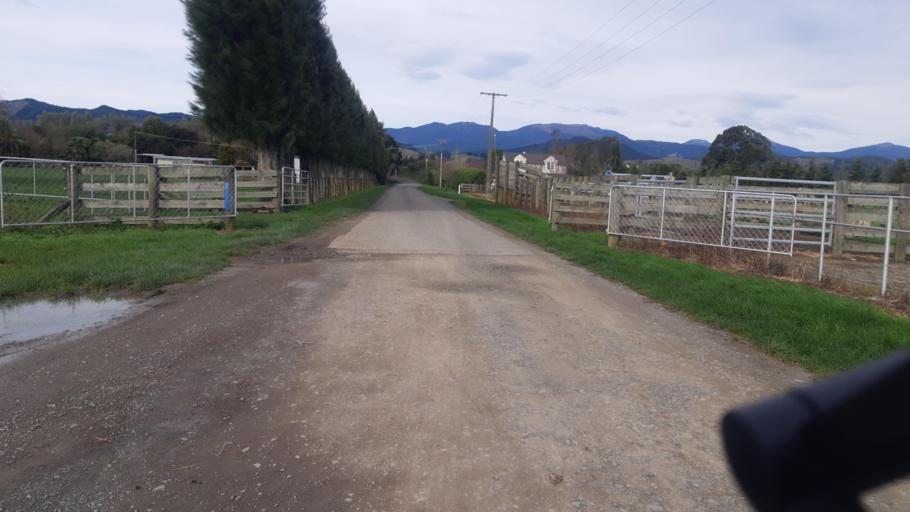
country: NZ
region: Tasman
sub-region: Tasman District
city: Brightwater
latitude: -41.3572
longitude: 173.1193
